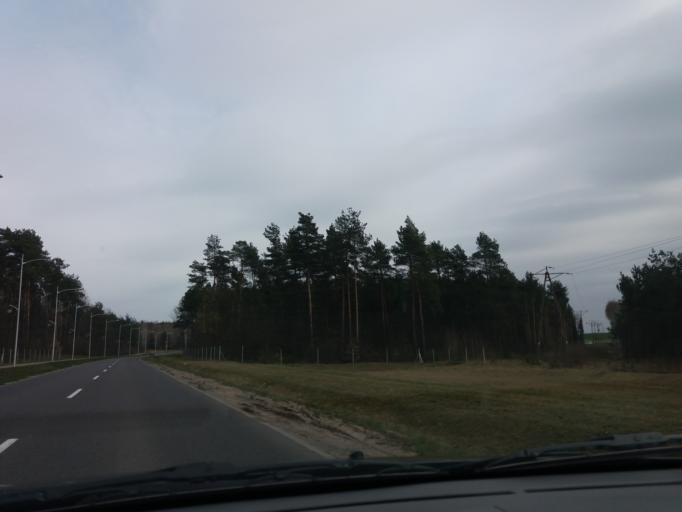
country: PL
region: Masovian Voivodeship
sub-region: Powiat mlawski
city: Mlawa
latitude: 53.1314
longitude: 20.3905
